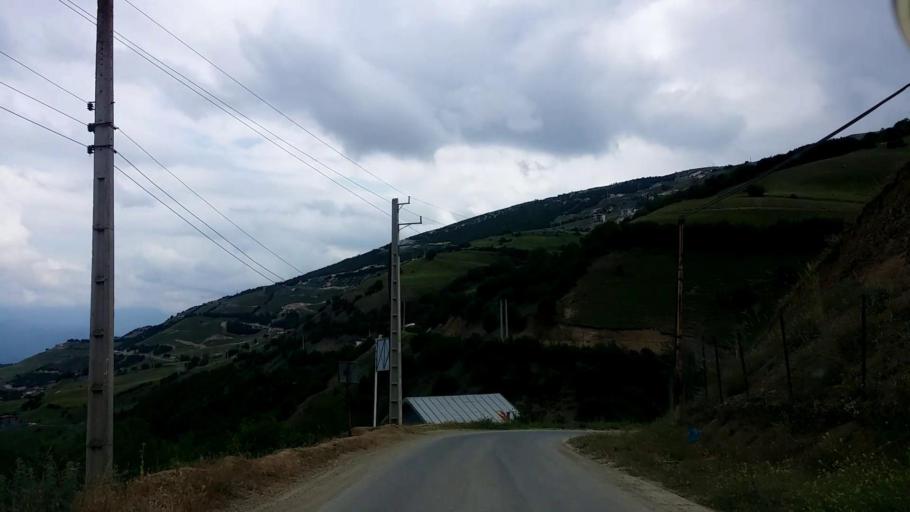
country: IR
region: Mazandaran
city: Chalus
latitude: 36.5537
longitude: 51.2708
